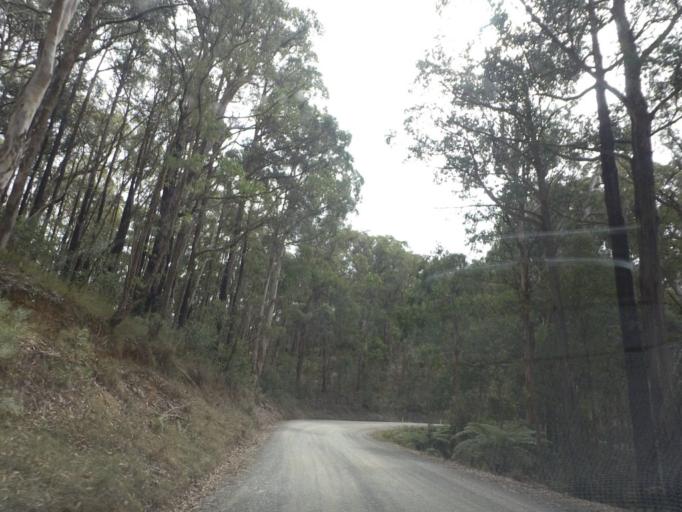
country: AU
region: Victoria
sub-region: Murrindindi
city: Alexandra
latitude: -37.4689
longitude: 145.9737
